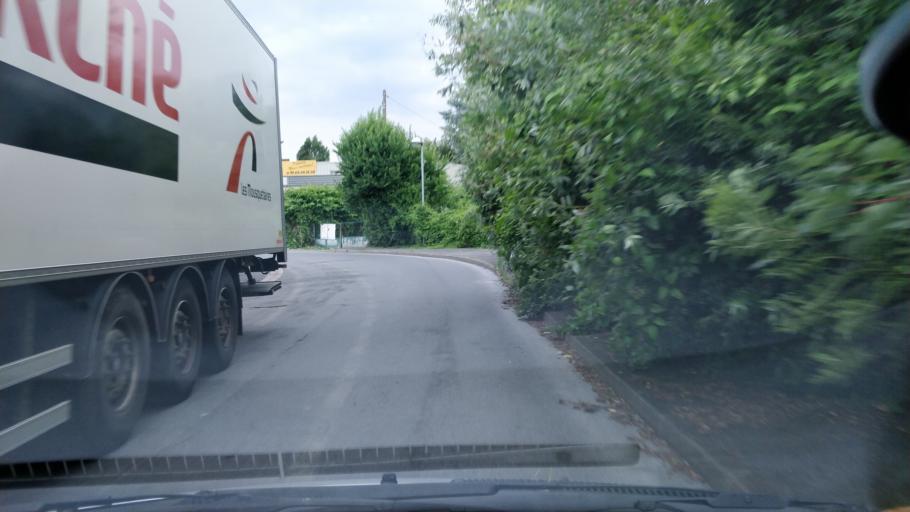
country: FR
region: Ile-de-France
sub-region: Departement de Seine-Saint-Denis
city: Montfermeil
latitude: 48.8929
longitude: 2.5810
